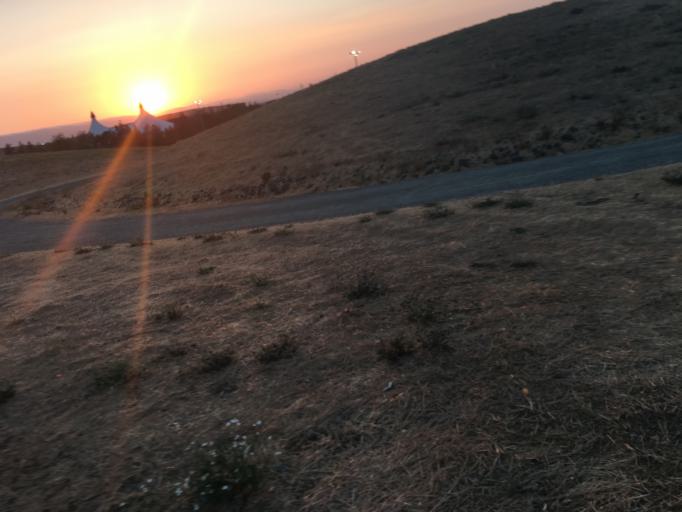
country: US
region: California
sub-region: Santa Clara County
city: Mountain View
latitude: 37.4257
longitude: -122.0744
